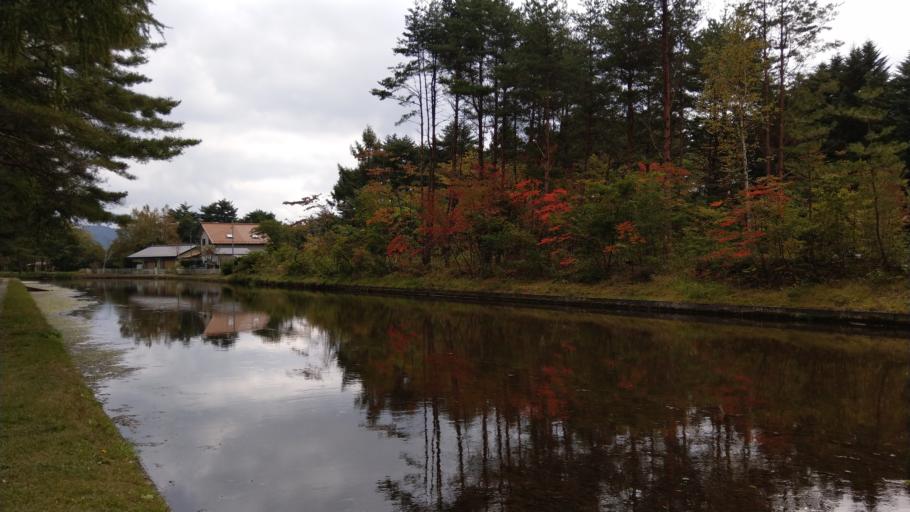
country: JP
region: Nagano
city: Komoro
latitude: 36.3302
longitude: 138.5276
